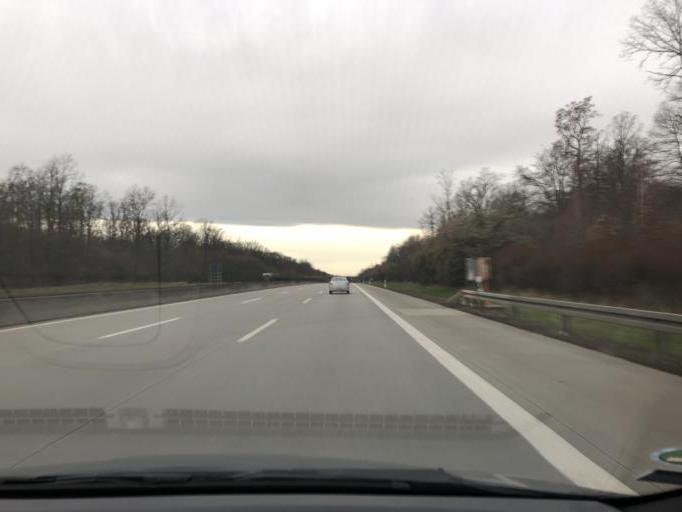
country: DE
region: Thuringia
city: Klettbach
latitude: 50.9184
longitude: 11.1062
